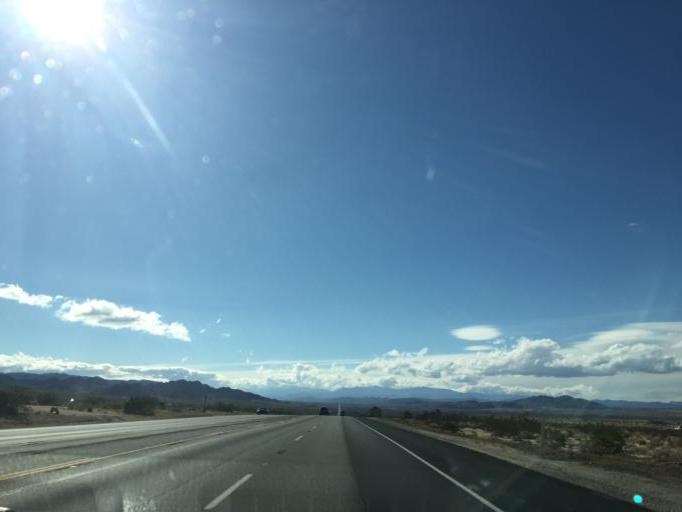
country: US
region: California
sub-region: San Bernardino County
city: Joshua Tree
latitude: 34.1352
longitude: -116.2041
